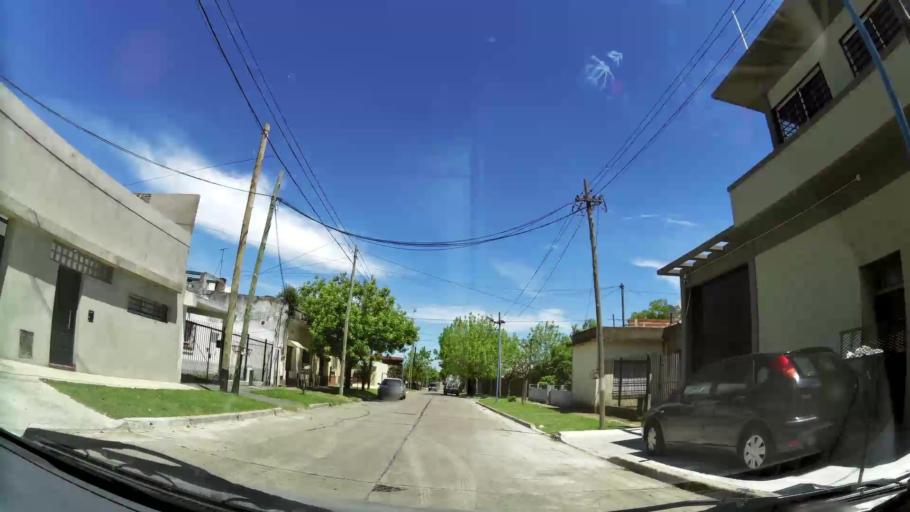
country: AR
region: Buenos Aires
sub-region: Partido de Quilmes
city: Quilmes
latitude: -34.7441
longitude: -58.2787
